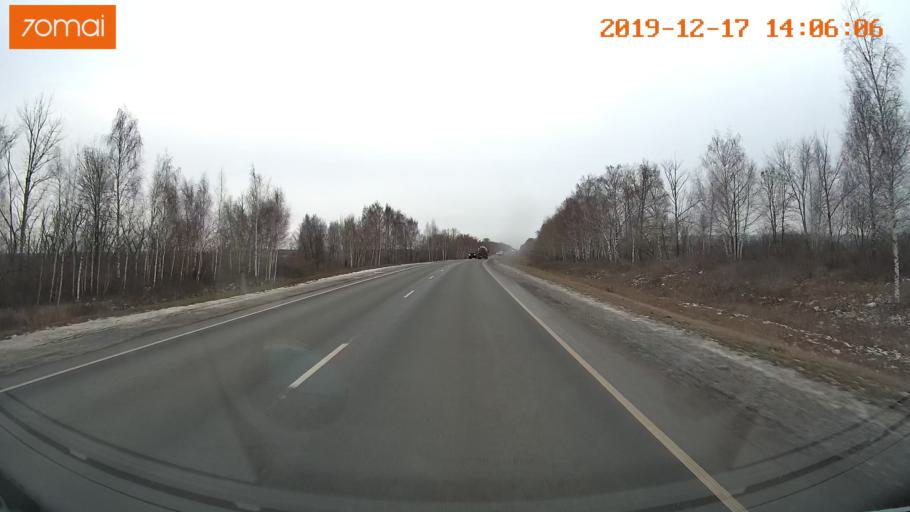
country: RU
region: Rjazan
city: Ryazan'
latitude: 54.5840
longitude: 39.5965
